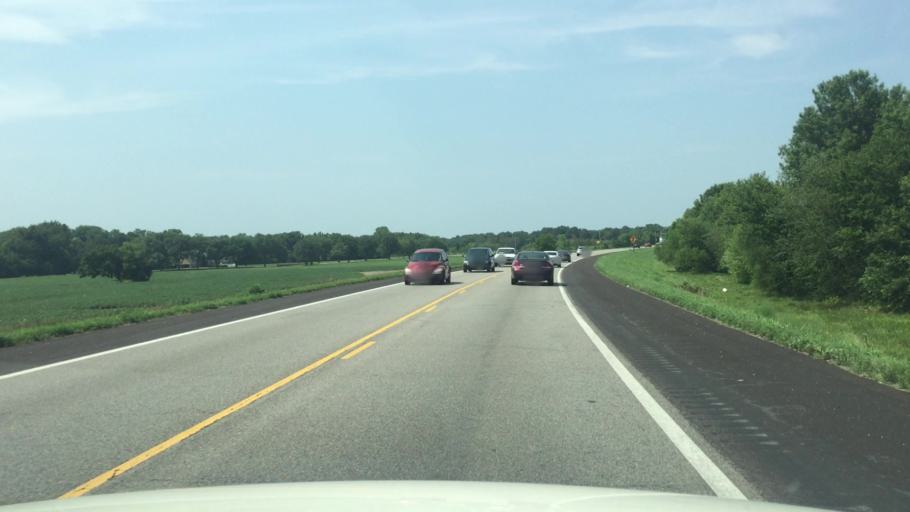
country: US
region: Kansas
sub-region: Crawford County
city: Pittsburg
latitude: 37.3917
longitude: -94.7162
